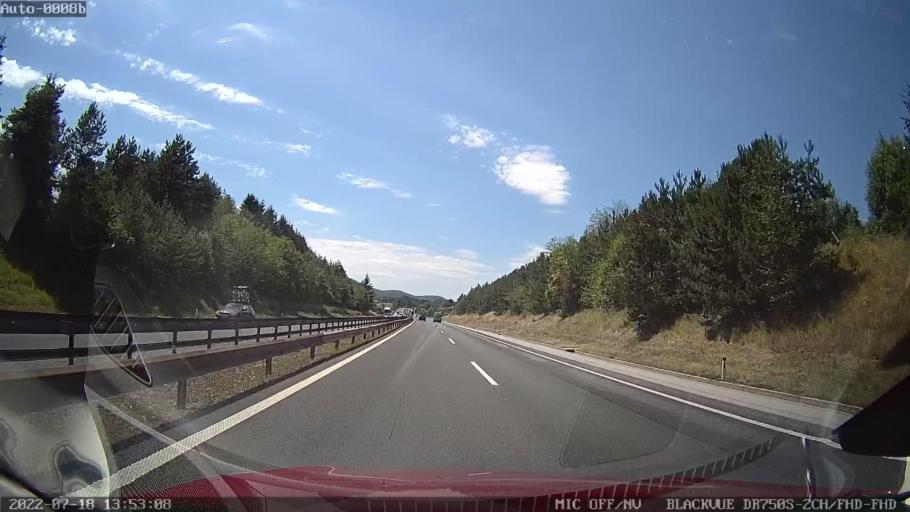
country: SI
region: Postojna
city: Postojna
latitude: 45.7630
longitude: 14.1094
